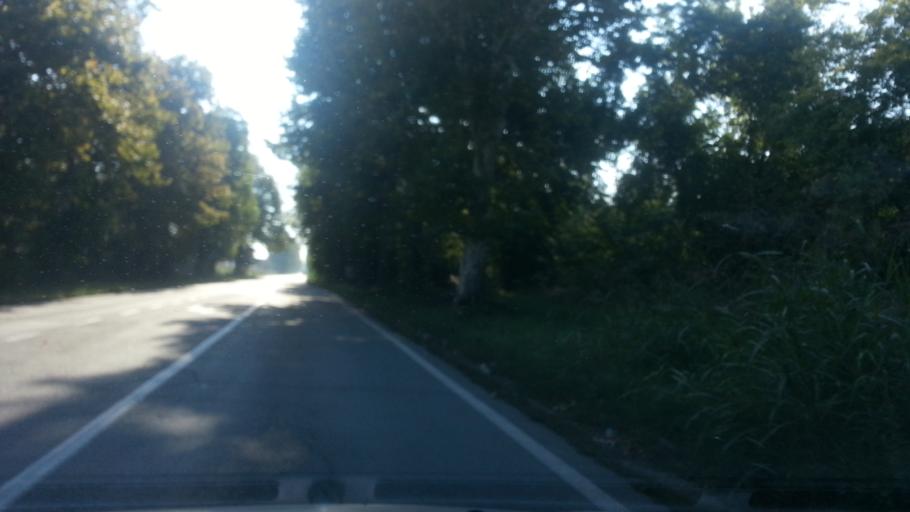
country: RS
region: Central Serbia
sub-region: Belgrade
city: Zemun
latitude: 44.8748
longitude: 20.3417
